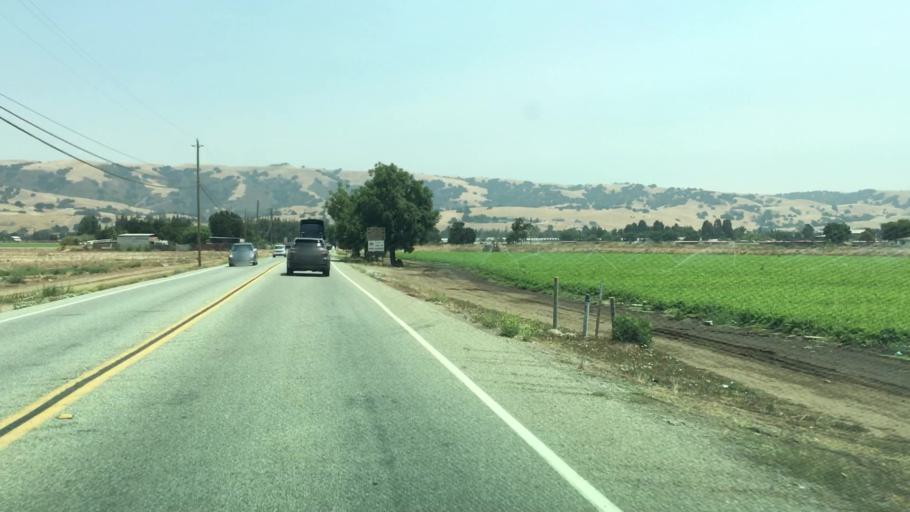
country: US
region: California
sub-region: Santa Clara County
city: Gilroy
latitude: 37.0323
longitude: -121.5408
